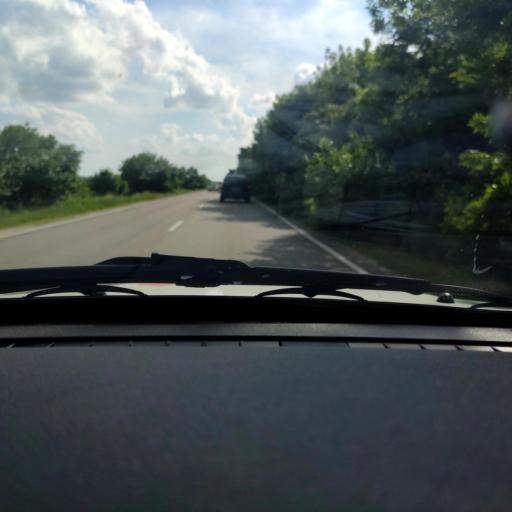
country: RU
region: Voronezj
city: Volya
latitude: 51.6970
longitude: 39.5079
